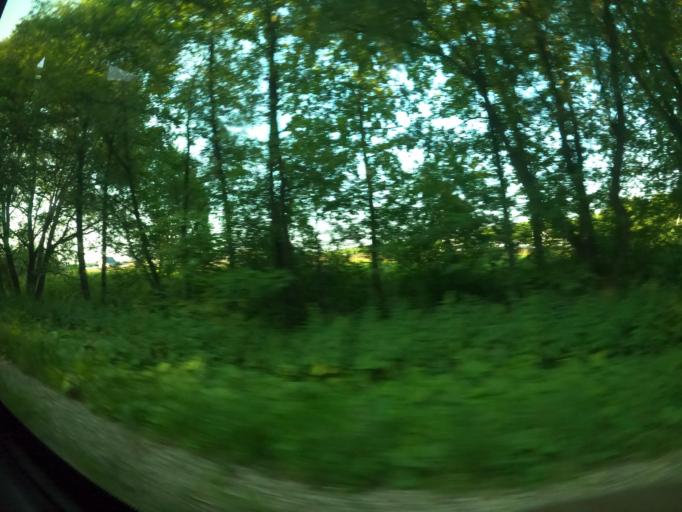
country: RU
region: Moskovskaya
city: Obolensk
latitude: 54.9421
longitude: 37.2405
